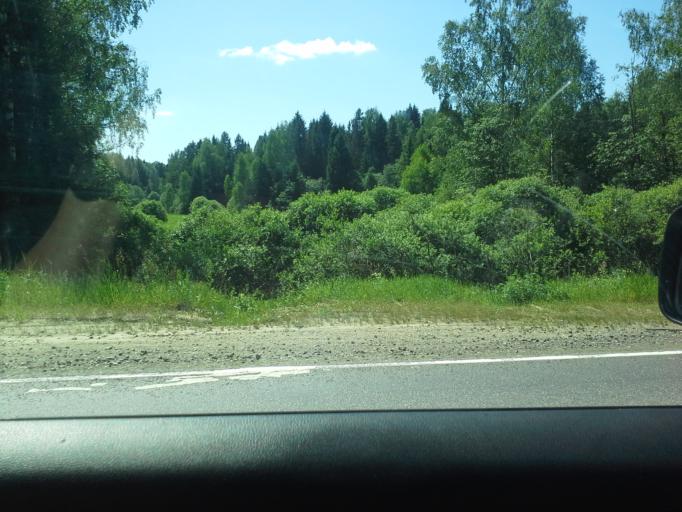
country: RU
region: Vladimir
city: Arsaki
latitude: 56.2786
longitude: 38.4053
